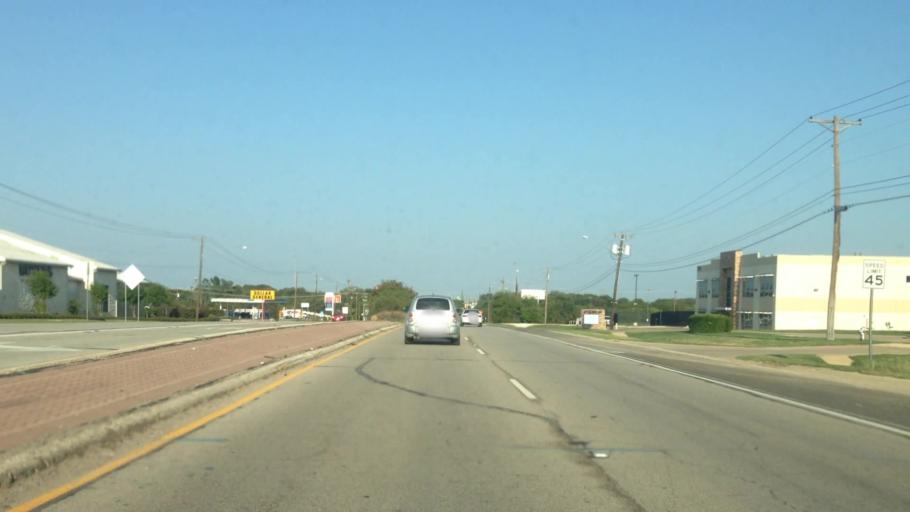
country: US
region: Texas
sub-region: Tarrant County
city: Richland Hills
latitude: 32.8090
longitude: -97.2196
